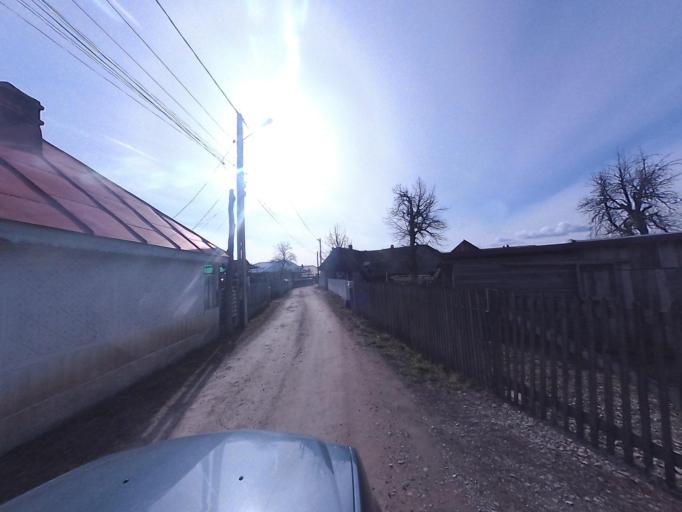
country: RO
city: Vanatori-Neamt
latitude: 47.2139
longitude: 26.3352
